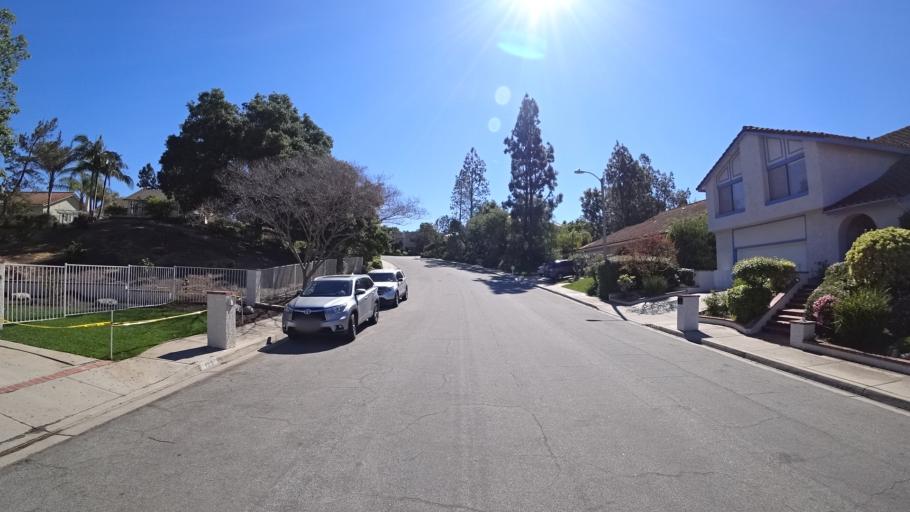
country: US
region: California
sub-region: Ventura County
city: Thousand Oaks
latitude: 34.1737
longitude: -118.8749
